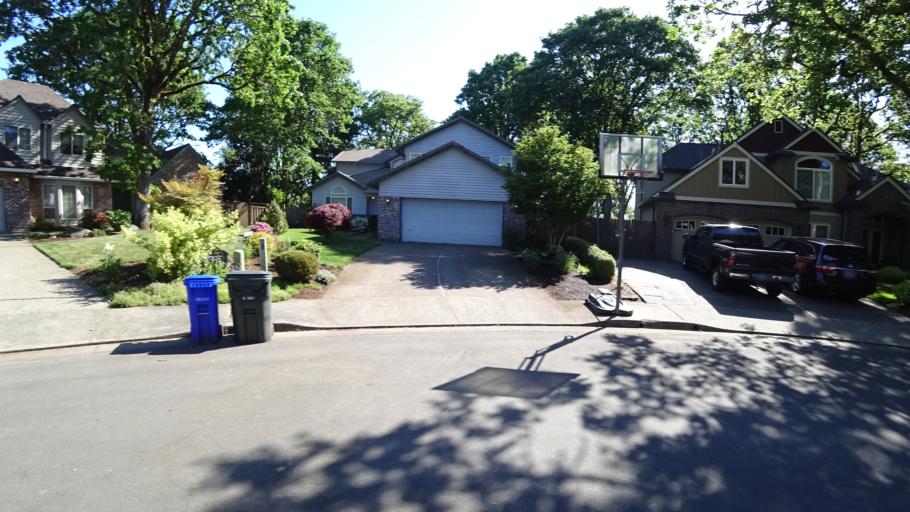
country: US
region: Oregon
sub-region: Washington County
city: Rockcreek
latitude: 45.5252
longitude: -122.9191
